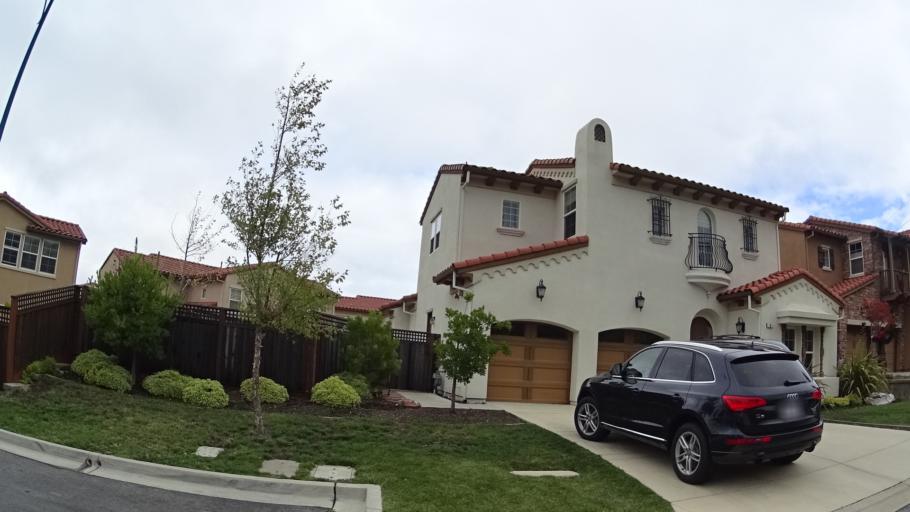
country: US
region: California
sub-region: San Mateo County
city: Millbrae
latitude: 37.5948
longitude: -122.4142
